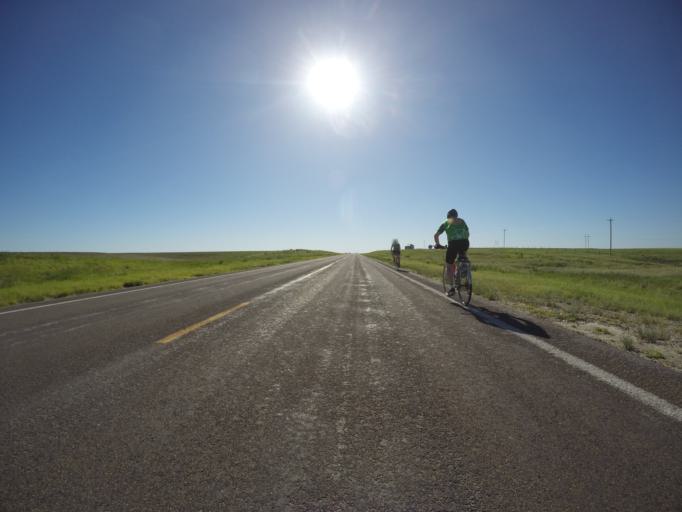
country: US
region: Kansas
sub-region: Norton County
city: Norton
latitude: 39.8281
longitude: -100.0365
